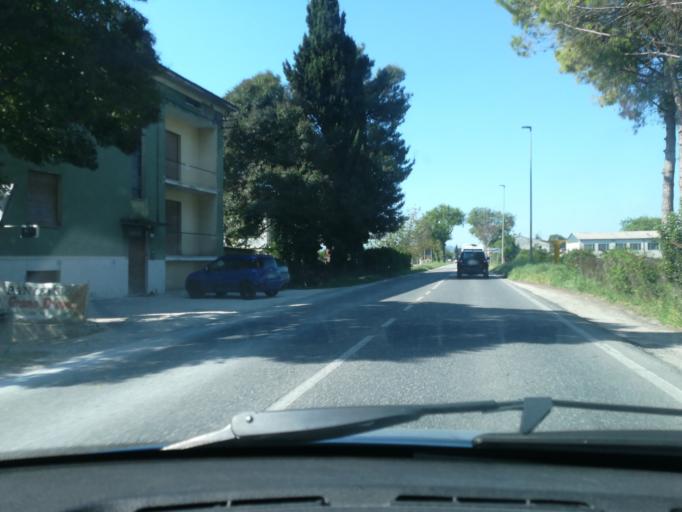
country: IT
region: The Marches
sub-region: Provincia di Macerata
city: Villa Potenza
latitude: 43.3267
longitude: 13.4205
